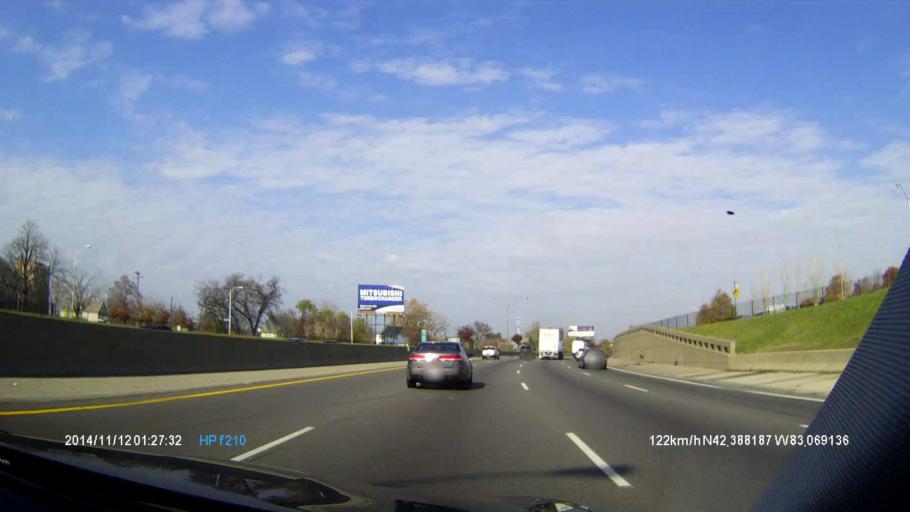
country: US
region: Michigan
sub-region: Wayne County
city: Hamtramck
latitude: 42.3883
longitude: -83.0691
